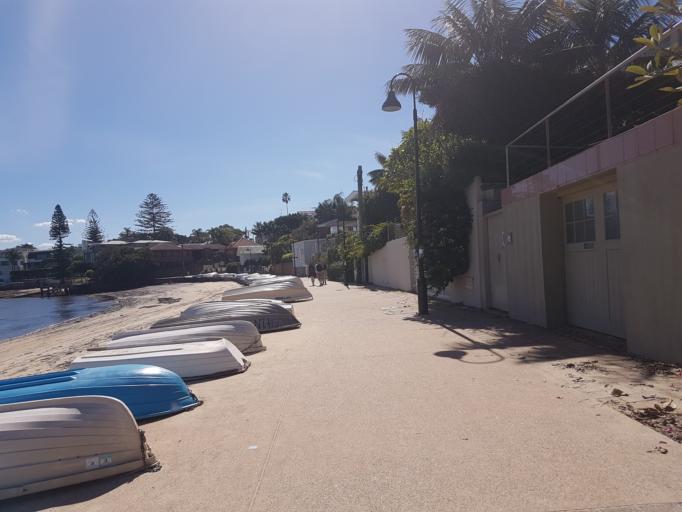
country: AU
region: New South Wales
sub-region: Waverley
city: Dover Heights
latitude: -33.8427
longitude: 151.2817
